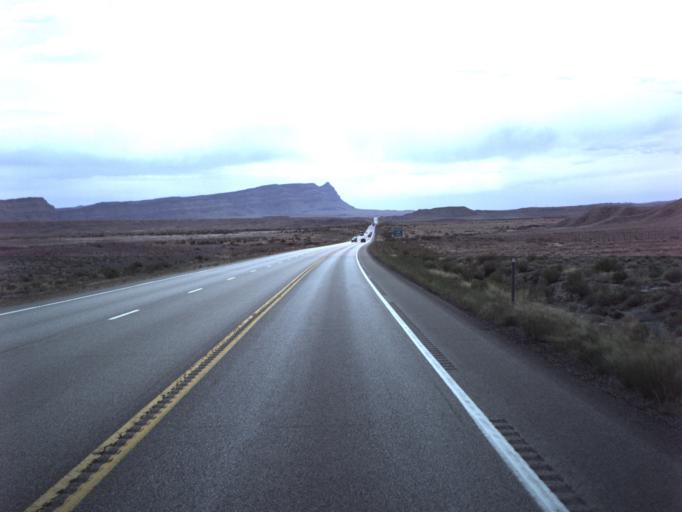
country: US
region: Utah
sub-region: Carbon County
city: East Carbon City
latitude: 39.3390
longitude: -110.3719
